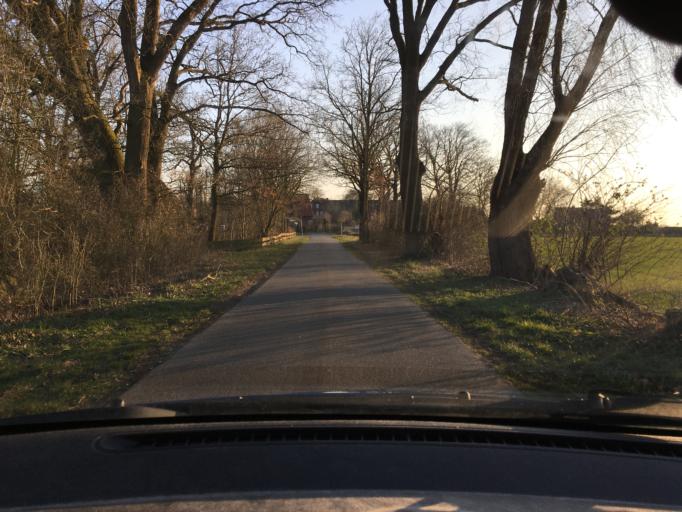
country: DE
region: Lower Saxony
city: Romstedt
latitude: 53.1510
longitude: 10.6644
